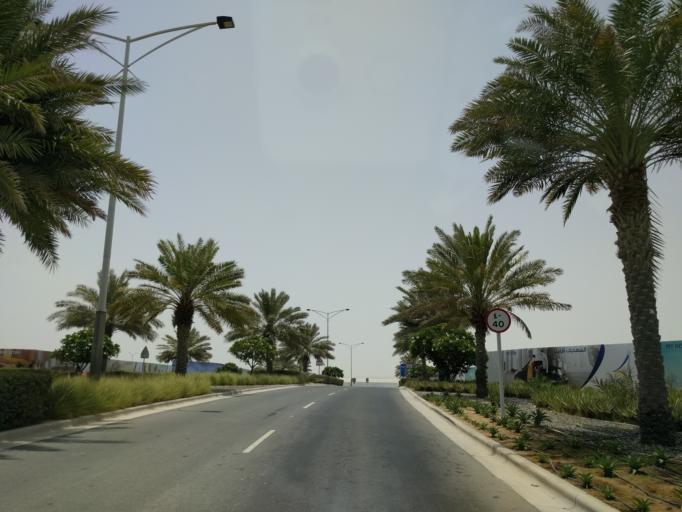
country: AE
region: Abu Dhabi
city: Abu Dhabi
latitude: 24.5425
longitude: 54.4416
